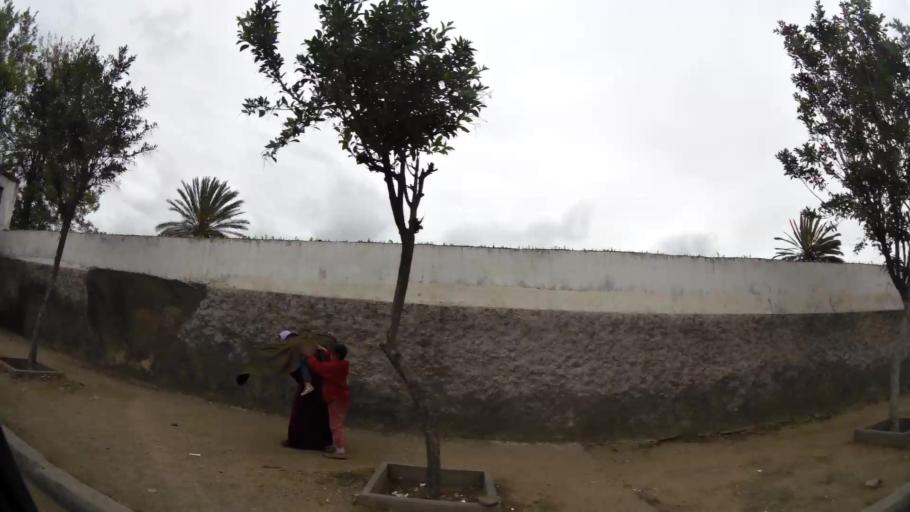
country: MA
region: Grand Casablanca
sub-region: Casablanca
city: Casablanca
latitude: 33.5661
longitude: -7.5639
